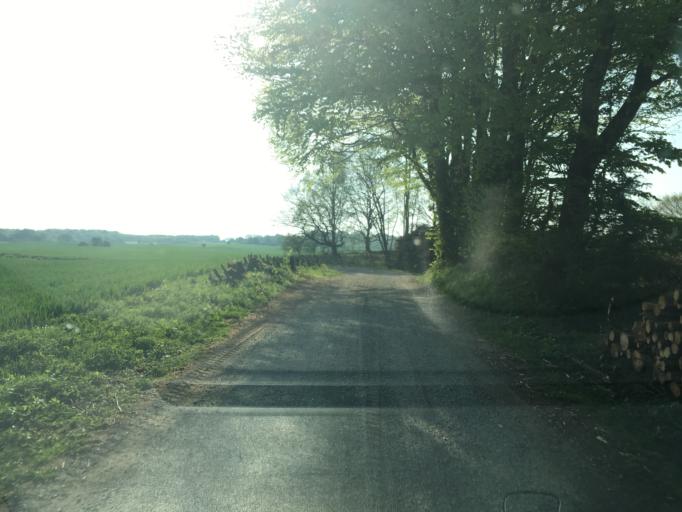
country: DK
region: South Denmark
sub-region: Aabenraa Kommune
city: Lojt Kirkeby
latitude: 55.1561
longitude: 9.3873
